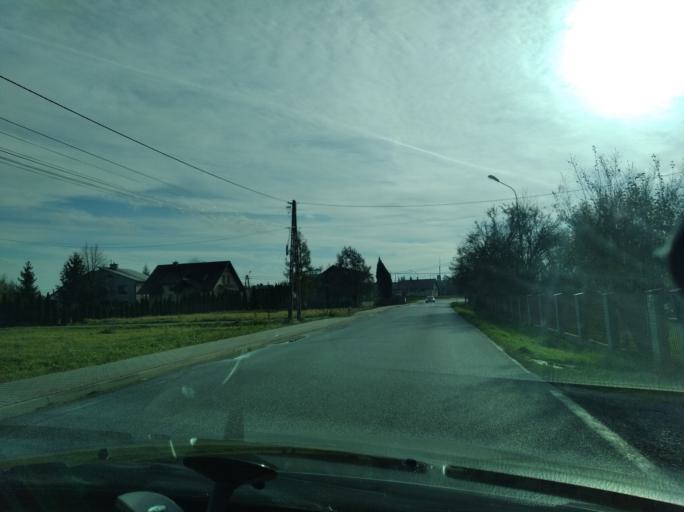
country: PL
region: Subcarpathian Voivodeship
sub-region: Powiat ropczycko-sedziszowski
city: Sedziszow Malopolski
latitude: 50.0774
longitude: 21.6986
